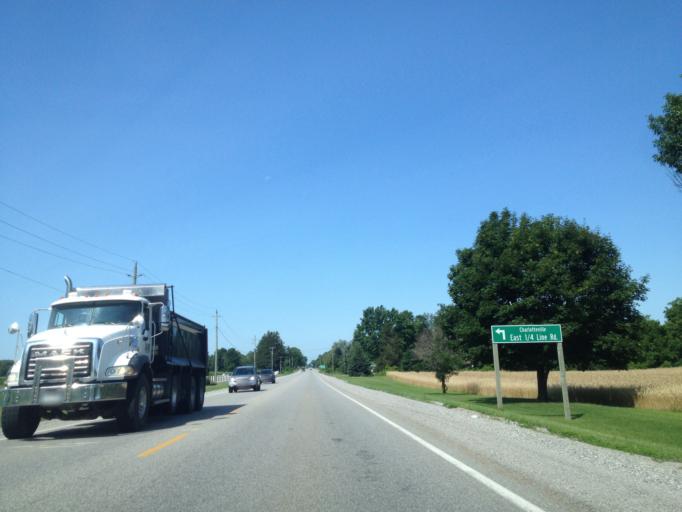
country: CA
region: Ontario
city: Norfolk County
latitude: 42.8327
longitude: -80.3829
